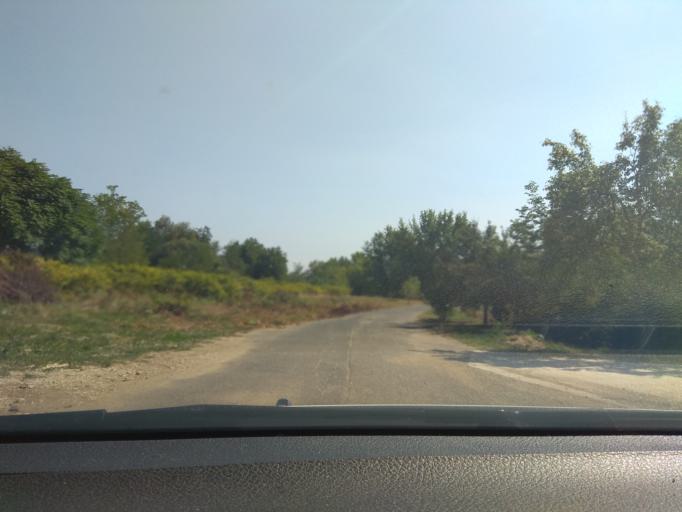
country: HU
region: Borsod-Abauj-Zemplen
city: Miskolc
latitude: 48.0772
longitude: 20.7877
